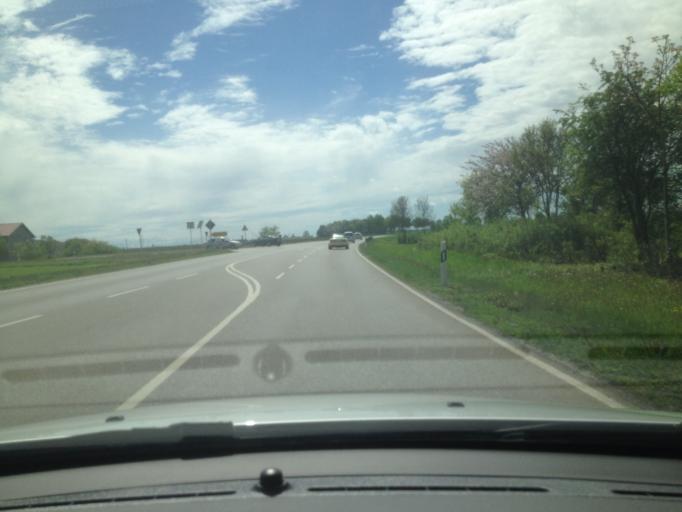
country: DE
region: Bavaria
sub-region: Swabia
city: Bobingen
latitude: 48.2573
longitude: 10.8432
